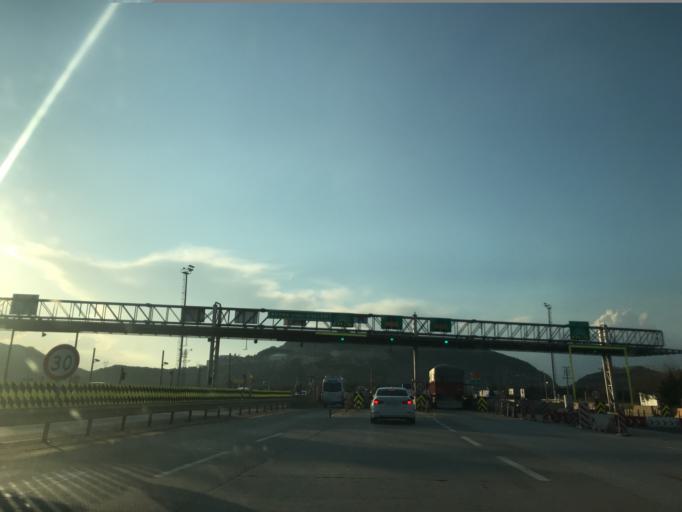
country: TR
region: Adana
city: Ceyhan
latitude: 36.9885
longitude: 35.7511
